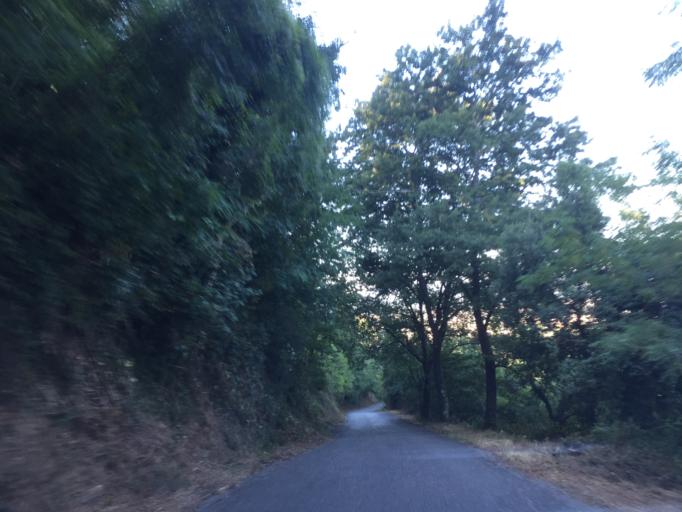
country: IT
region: Tuscany
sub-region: Provincia di Pistoia
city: Pistoia
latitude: 43.9478
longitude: 10.9573
